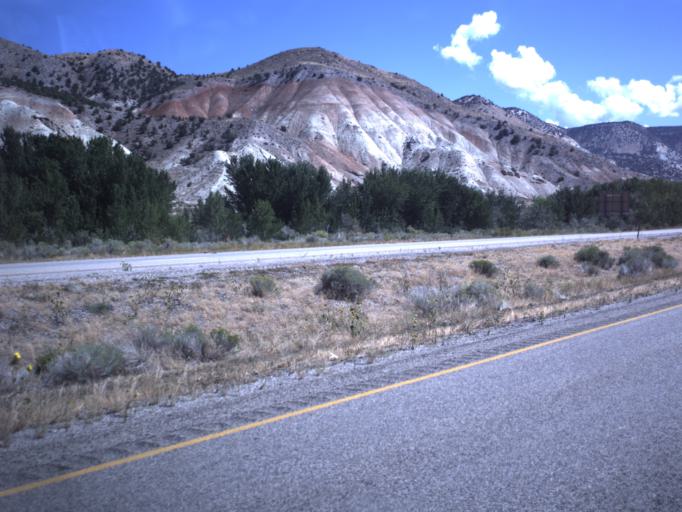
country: US
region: Utah
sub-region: Sevier County
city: Salina
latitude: 38.9303
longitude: -111.8345
